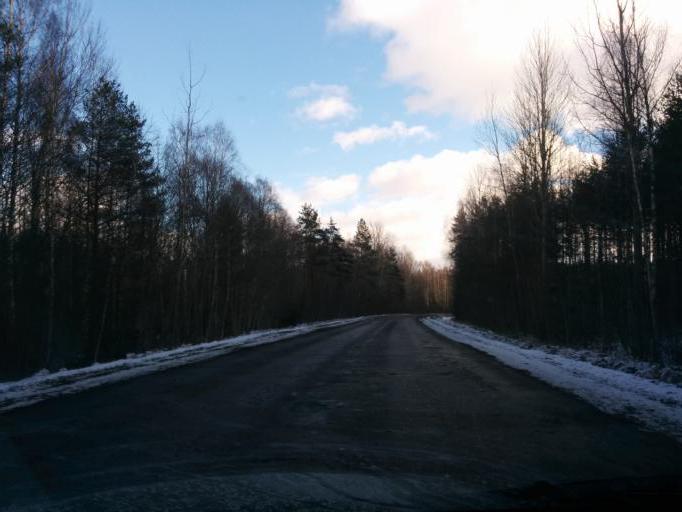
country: LV
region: Balvu Rajons
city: Balvi
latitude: 57.1751
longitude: 27.1253
